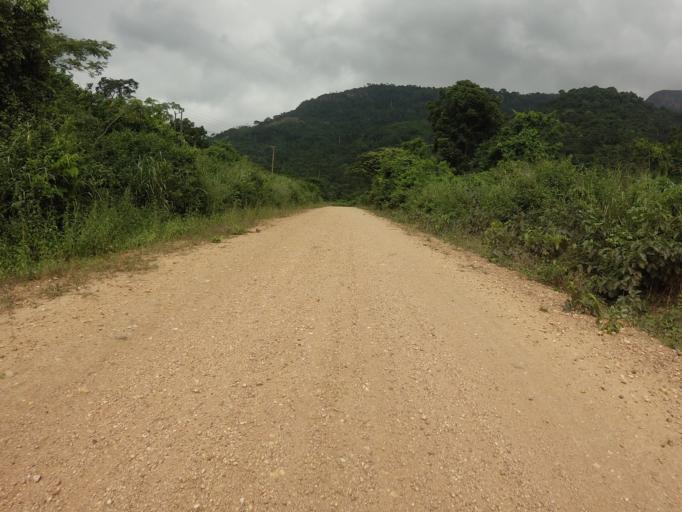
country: GH
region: Volta
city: Kpandu
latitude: 6.8724
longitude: 0.4250
